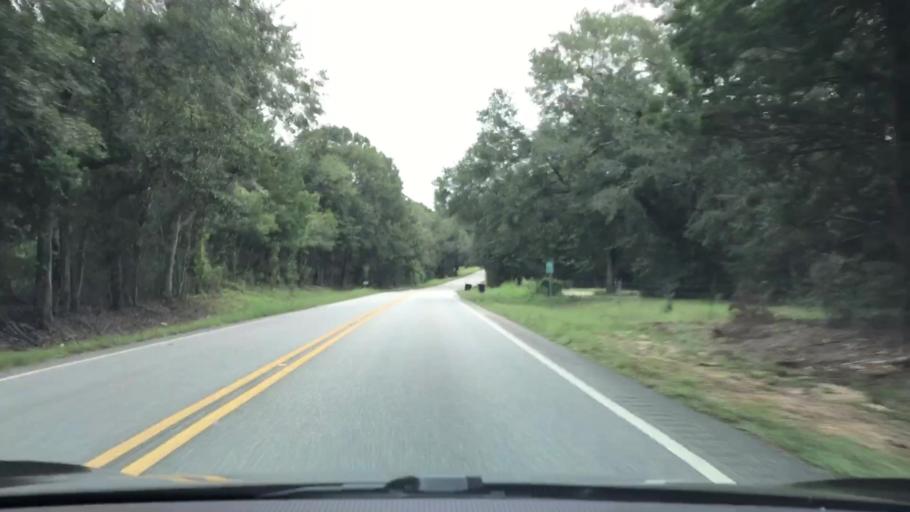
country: US
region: Alabama
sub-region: Geneva County
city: Samson
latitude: 31.0301
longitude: -86.1110
